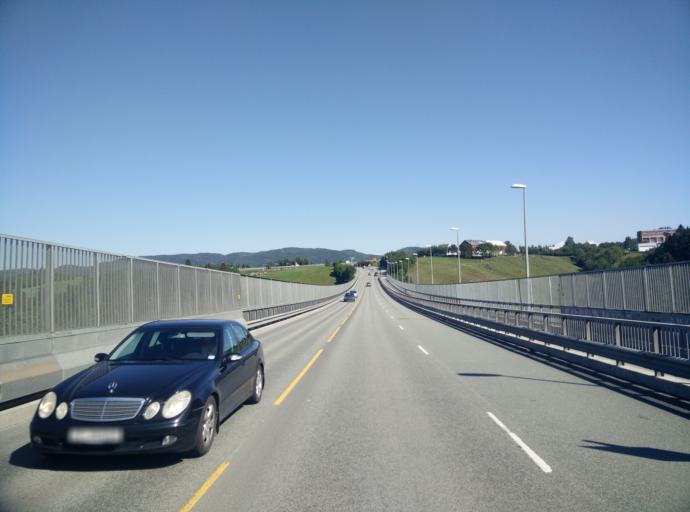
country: NO
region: Sor-Trondelag
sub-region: Trondheim
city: Trondheim
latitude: 63.3708
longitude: 10.3654
